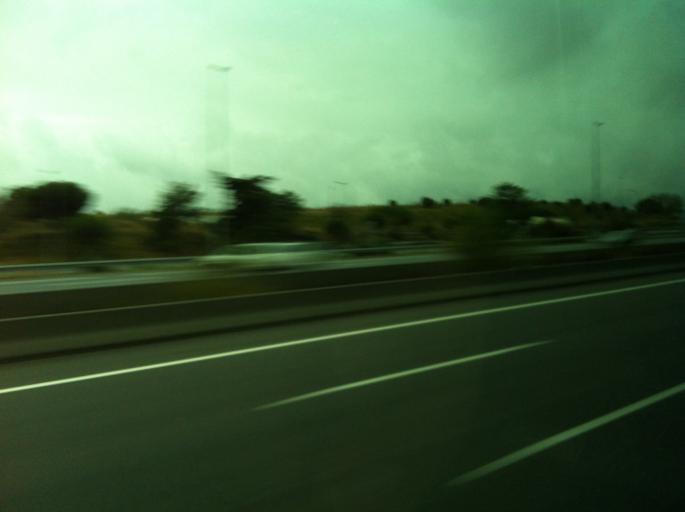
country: ES
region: Madrid
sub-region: Provincia de Madrid
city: Alpedrete
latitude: 40.6434
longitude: -4.0407
